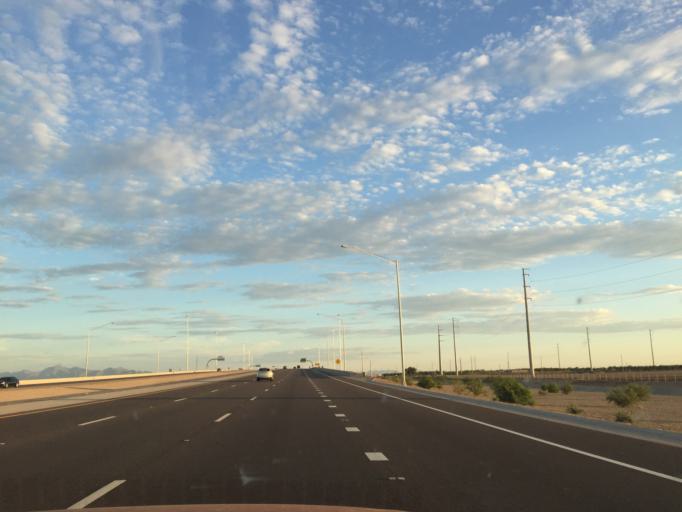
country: US
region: Arizona
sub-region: Maricopa County
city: Citrus Park
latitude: 33.5719
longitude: -112.4184
